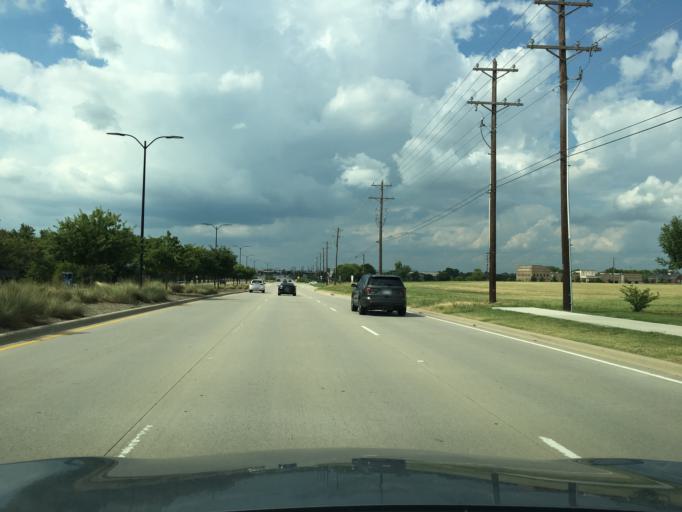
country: US
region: Texas
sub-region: Denton County
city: Little Elm
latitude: 33.1608
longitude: -96.8907
